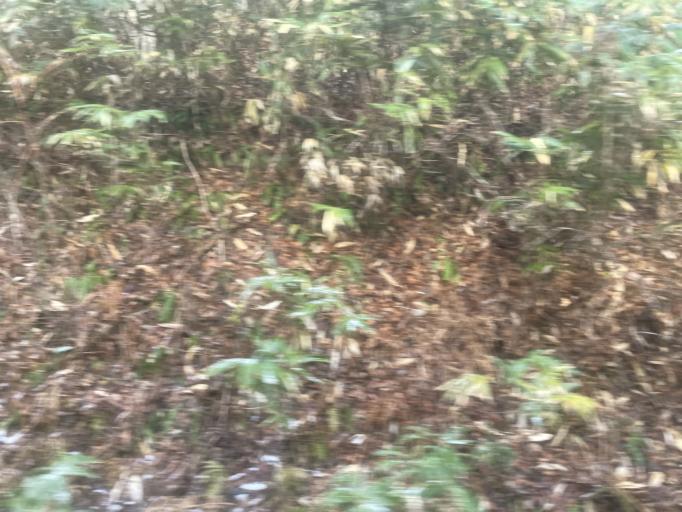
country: JP
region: Aomori
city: Goshogawara
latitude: 41.0788
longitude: 140.5292
